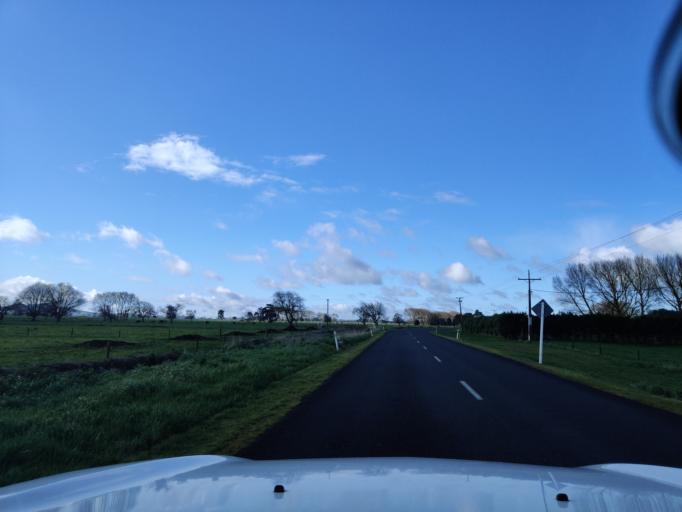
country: NZ
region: Waikato
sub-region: Waikato District
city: Ngaruawahia
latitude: -37.5865
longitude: 175.2861
